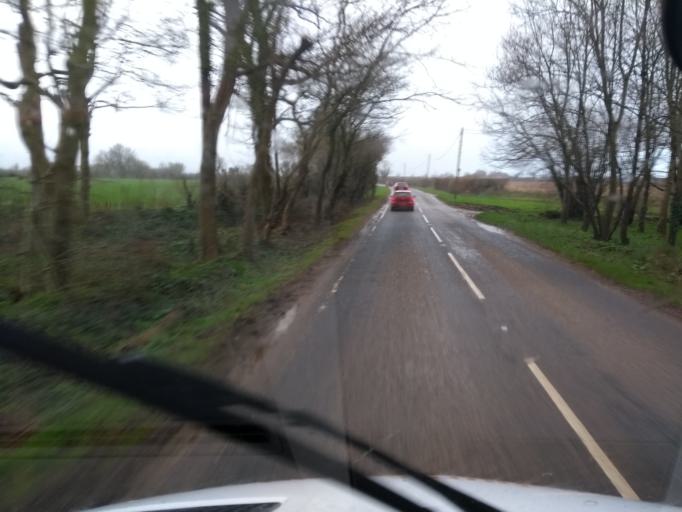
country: GB
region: England
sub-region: Somerset
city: Castle Cary
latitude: 51.0807
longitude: -2.4944
